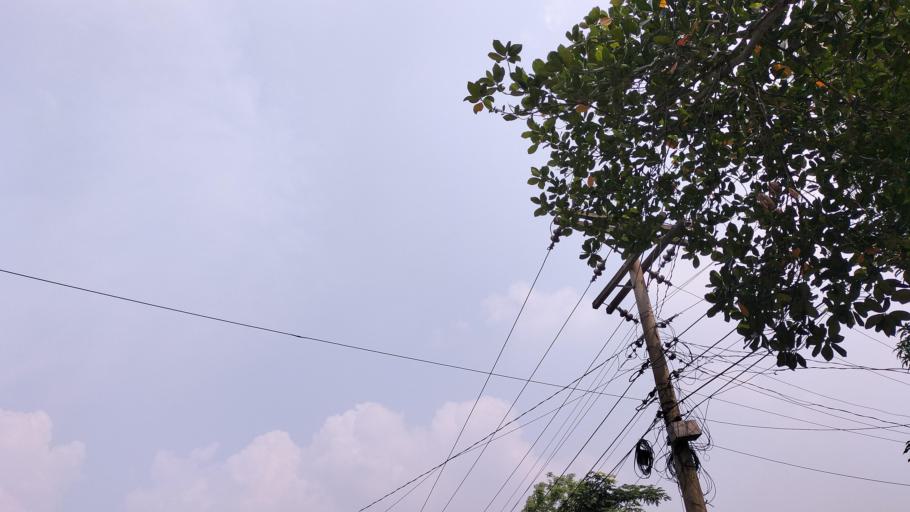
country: BD
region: Dhaka
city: Azimpur
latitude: 23.6953
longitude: 90.2993
